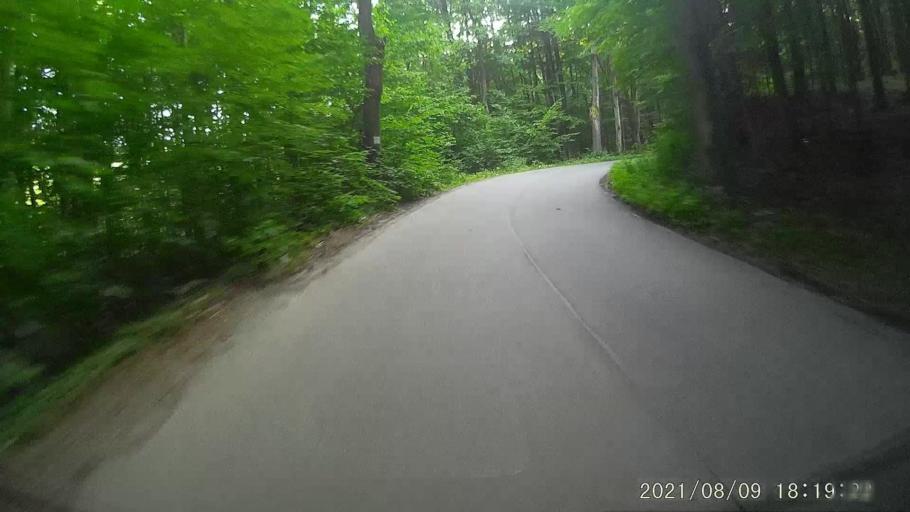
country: PL
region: Lower Silesian Voivodeship
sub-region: Powiat zabkowicki
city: Bardo
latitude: 50.5109
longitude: 16.6842
